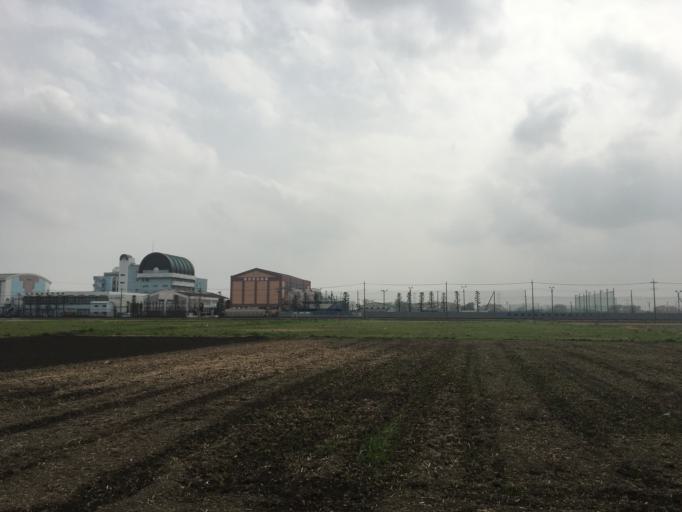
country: JP
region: Saitama
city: Kazo
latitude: 36.1093
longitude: 139.6271
